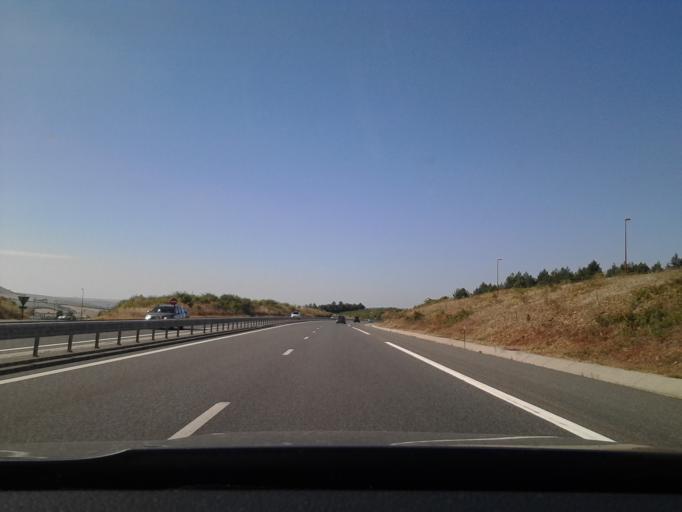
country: FR
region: Midi-Pyrenees
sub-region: Departement de l'Aveyron
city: Millau
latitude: 44.1712
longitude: 3.0311
